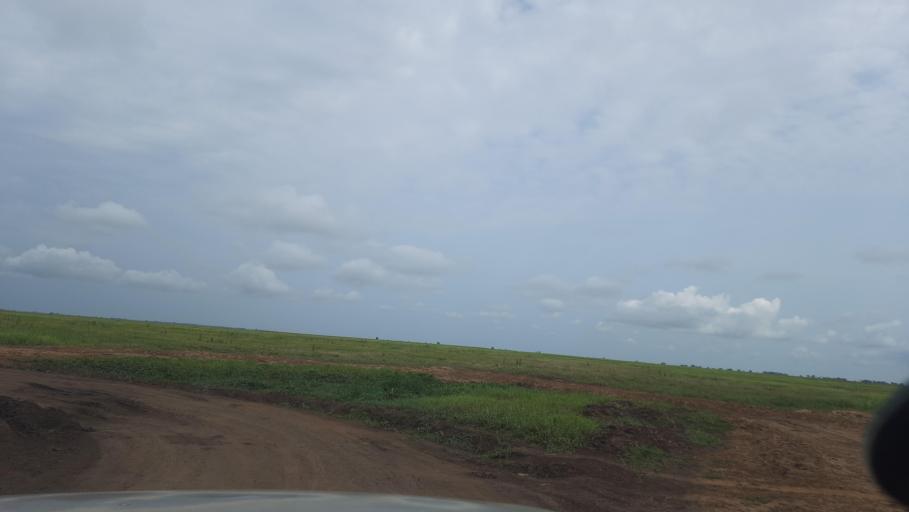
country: ET
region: Gambela
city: Gambela
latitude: 8.3388
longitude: 33.7765
